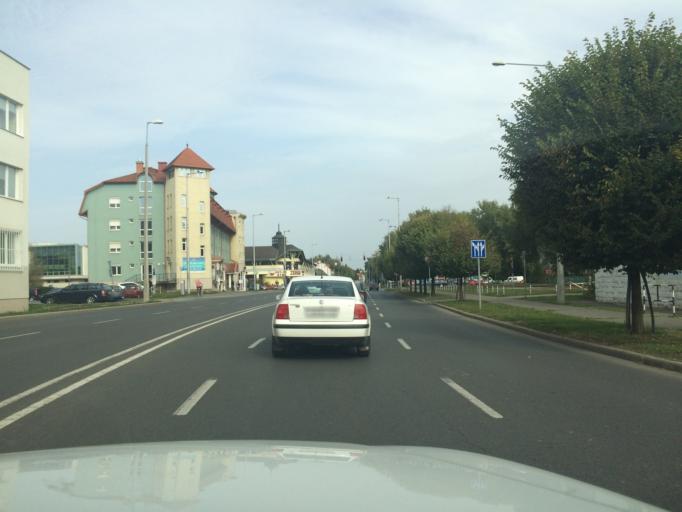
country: HU
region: Szabolcs-Szatmar-Bereg
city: Nyiregyhaza
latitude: 47.9564
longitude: 21.7207
